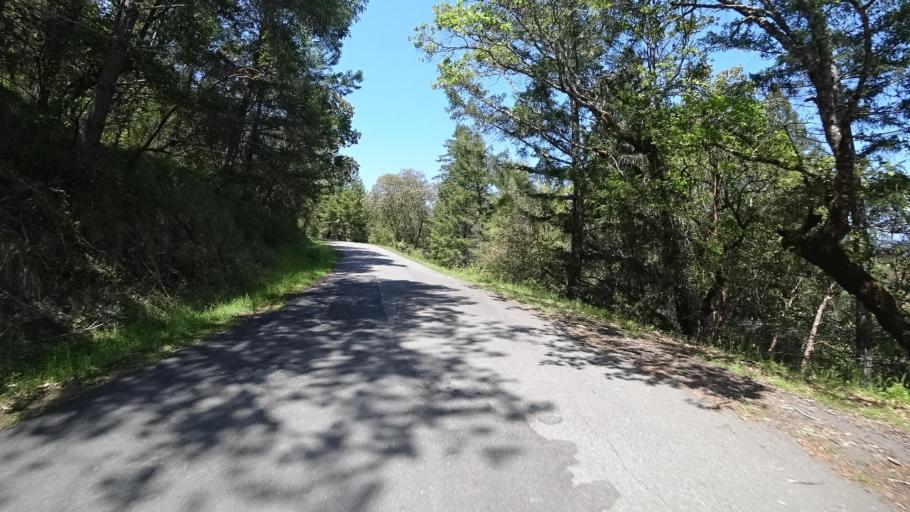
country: US
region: California
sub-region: Humboldt County
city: Redway
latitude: 40.2168
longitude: -123.6567
